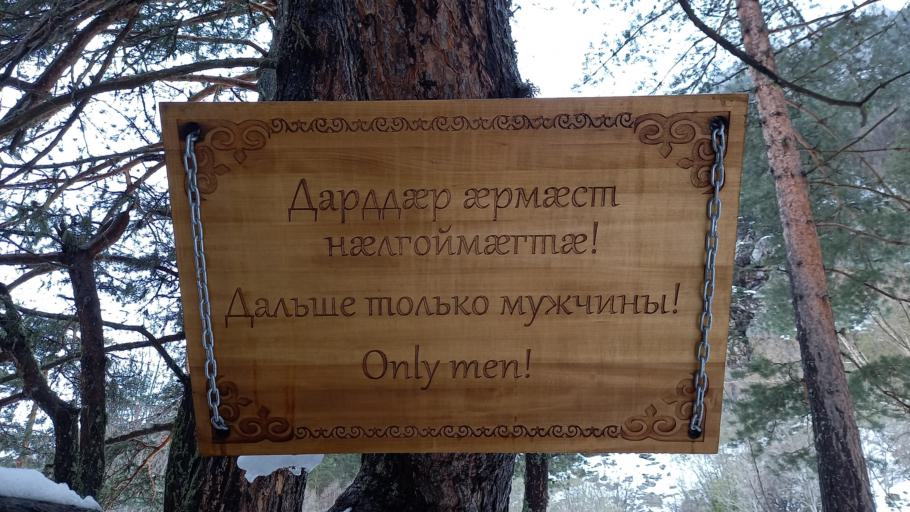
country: RU
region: North Ossetia
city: Mizur
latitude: 42.7907
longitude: 43.9055
